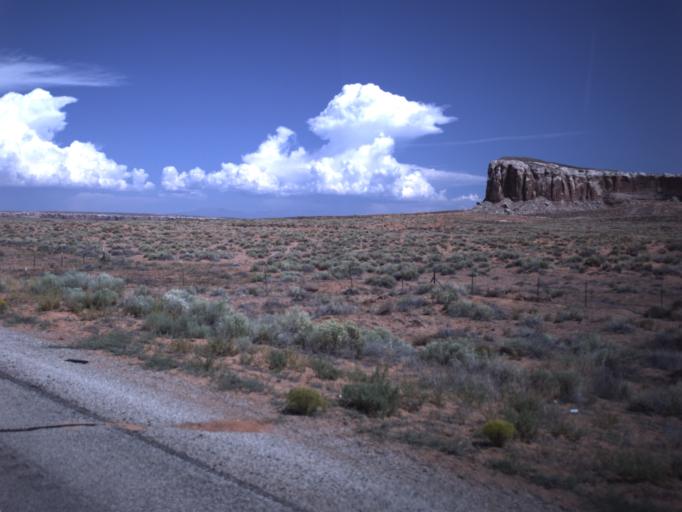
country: US
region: Utah
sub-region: San Juan County
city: Blanding
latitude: 37.2214
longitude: -109.6164
